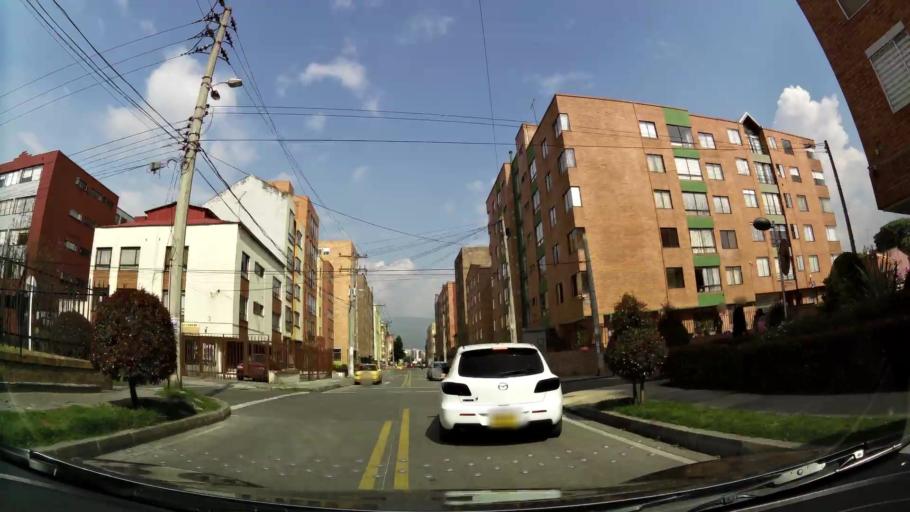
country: CO
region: Bogota D.C.
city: Barrio San Luis
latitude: 4.7317
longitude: -74.0531
